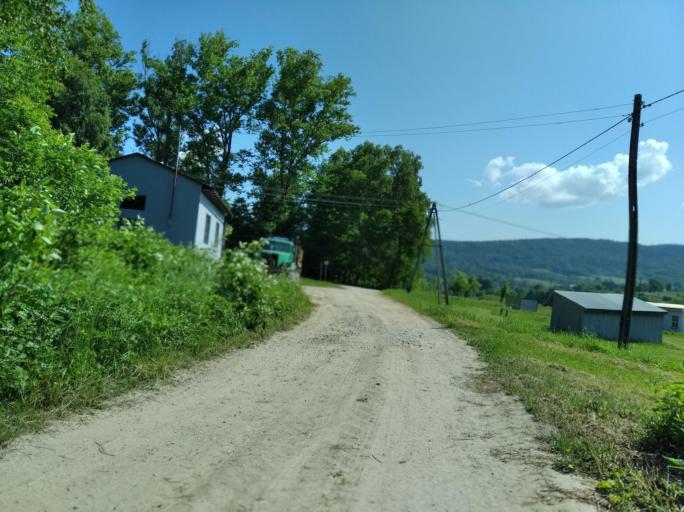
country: PL
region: Subcarpathian Voivodeship
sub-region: Powiat krosnienski
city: Odrzykon
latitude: 49.7719
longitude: 21.7624
